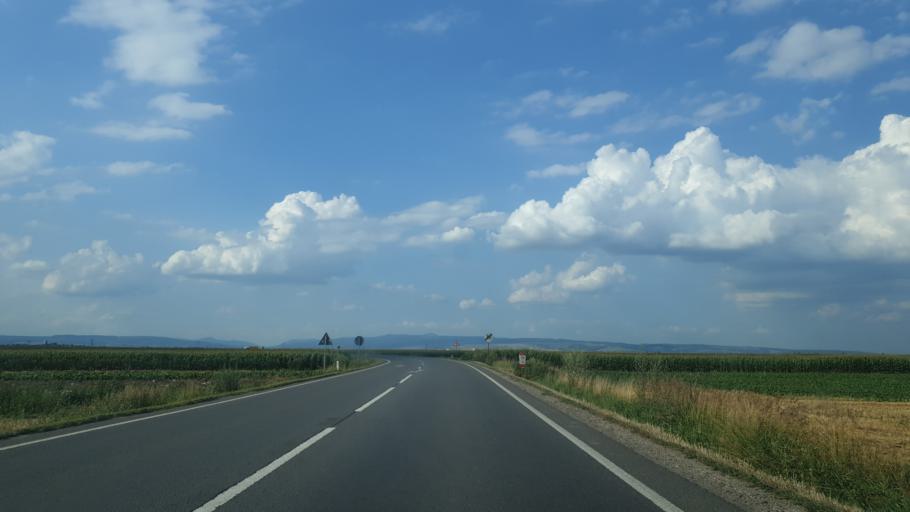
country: RO
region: Covasna
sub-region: Comuna Chichis
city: Chichis
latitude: 45.7827
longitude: 25.8067
